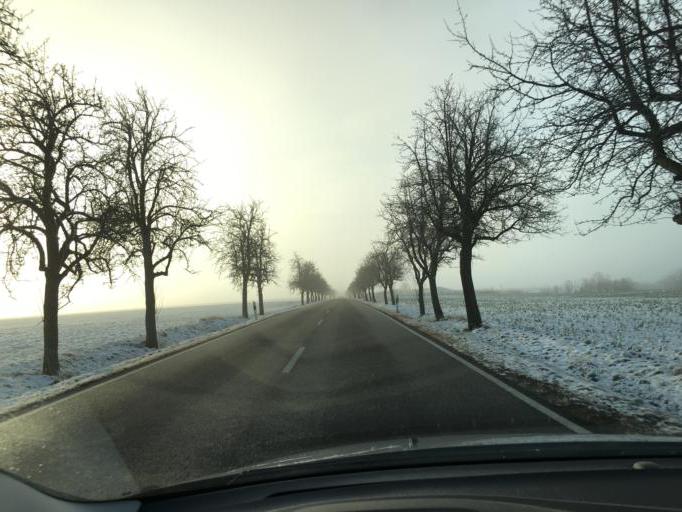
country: DE
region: Saxony
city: Geithain
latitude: 51.0451
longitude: 12.7173
